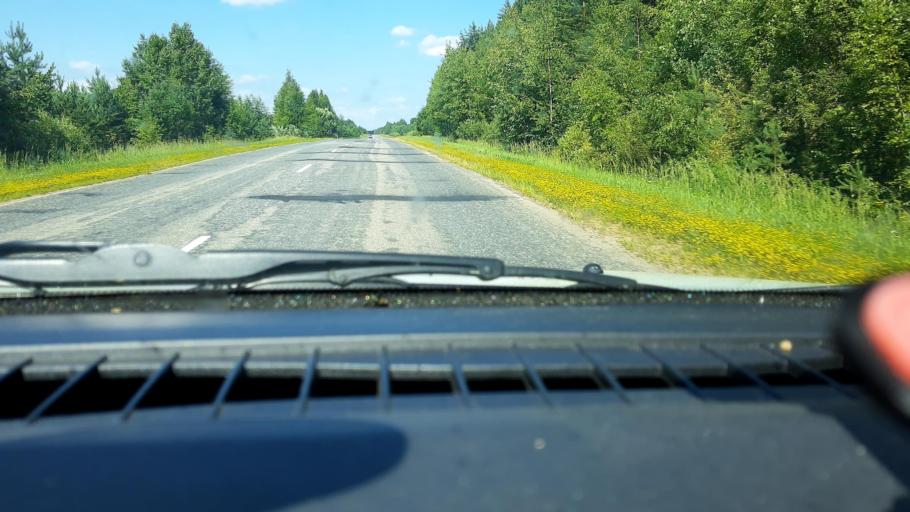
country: RU
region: Nizjnij Novgorod
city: Tonkino
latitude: 57.3097
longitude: 46.4663
